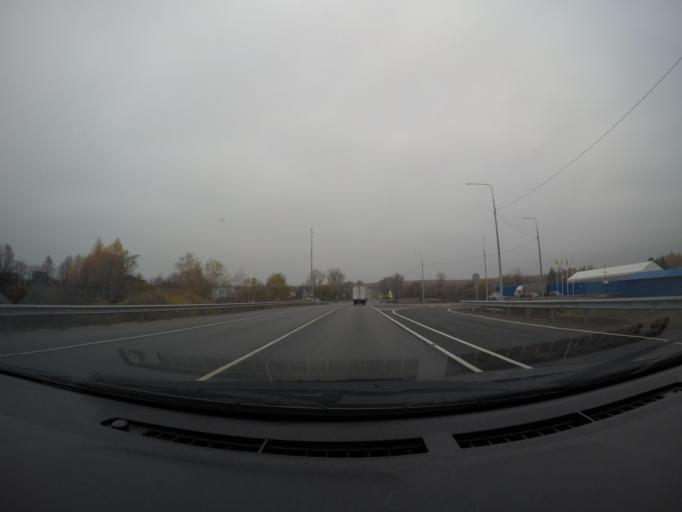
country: RU
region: Moskovskaya
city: Zhitnevo
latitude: 55.3632
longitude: 37.9939
